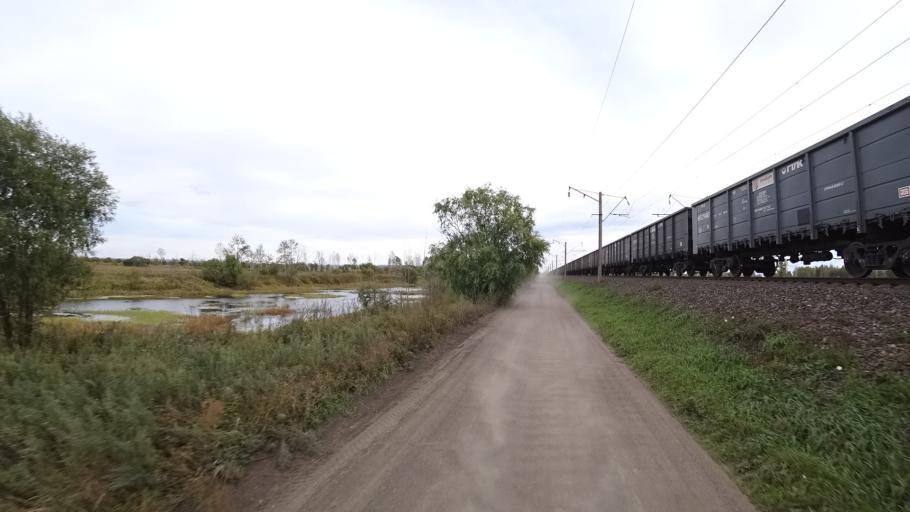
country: RU
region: Amur
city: Arkhara
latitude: 49.3633
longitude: 130.1472
